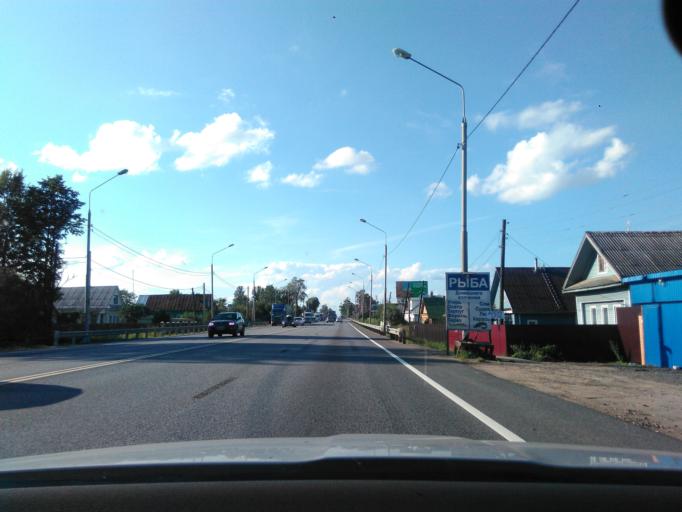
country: RU
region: Tverskaya
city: Zavidovo
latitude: 56.5268
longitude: 36.5295
